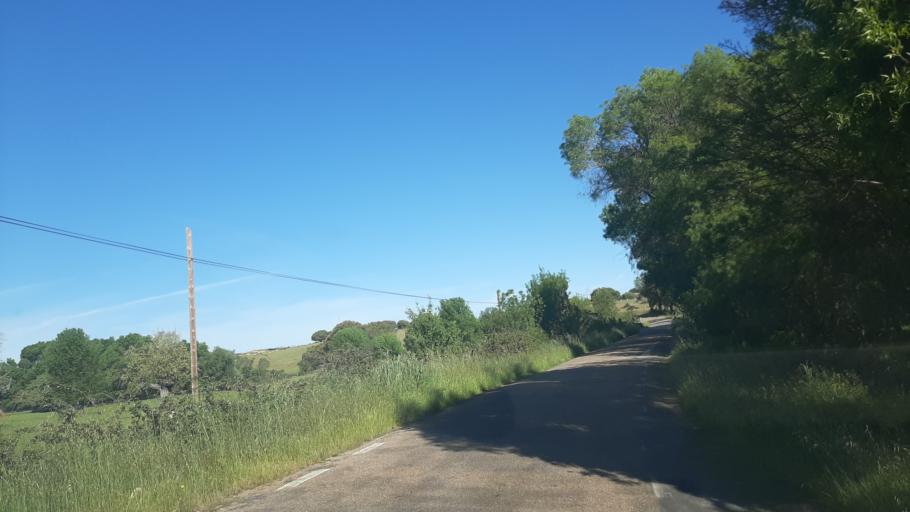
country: ES
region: Castille and Leon
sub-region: Provincia de Salamanca
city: Guijo de Avila
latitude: 40.5351
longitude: -5.6509
